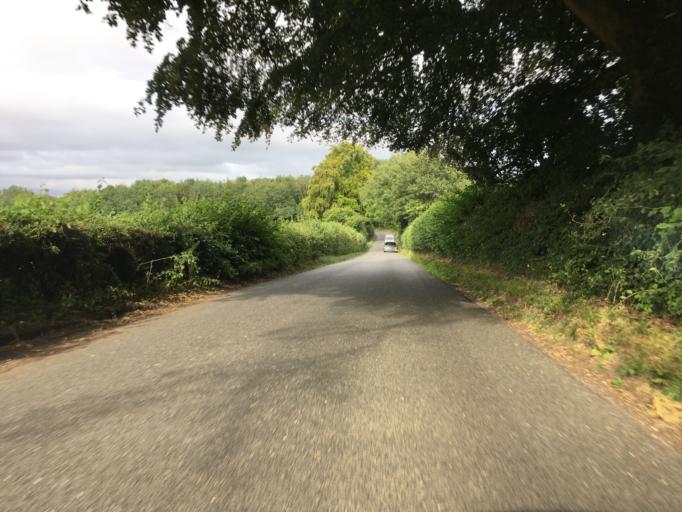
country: GB
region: England
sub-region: Hampshire
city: Colden Common
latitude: 51.0174
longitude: -1.2434
